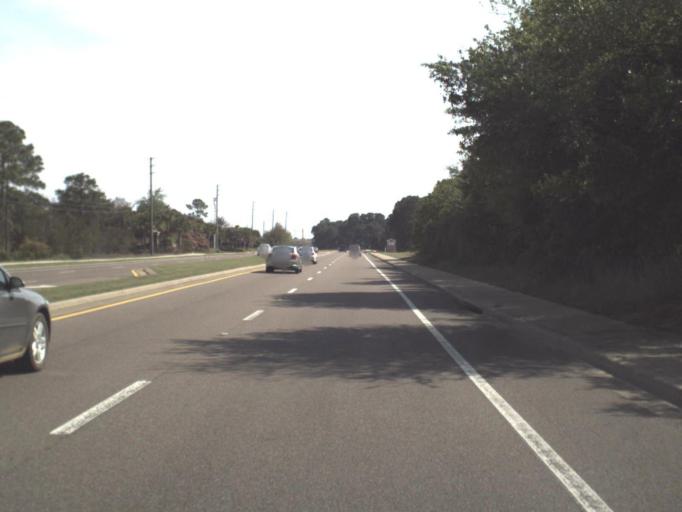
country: US
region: Florida
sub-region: Okaloosa County
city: Destin
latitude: 30.3981
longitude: -86.4274
